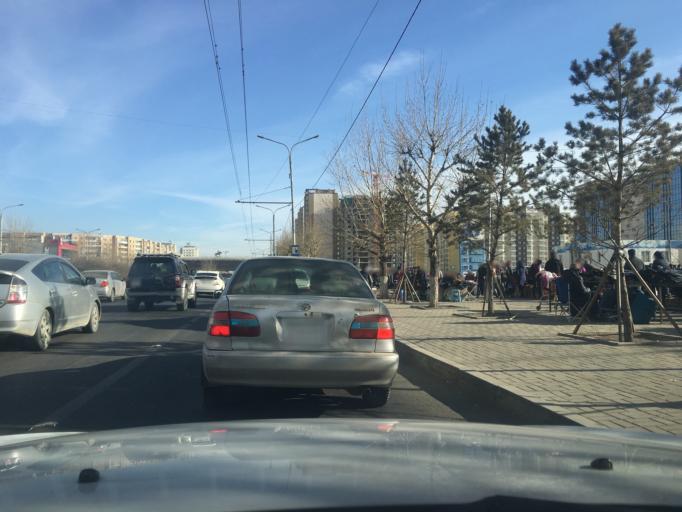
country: MN
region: Ulaanbaatar
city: Ulaanbaatar
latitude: 47.9112
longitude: 106.8342
